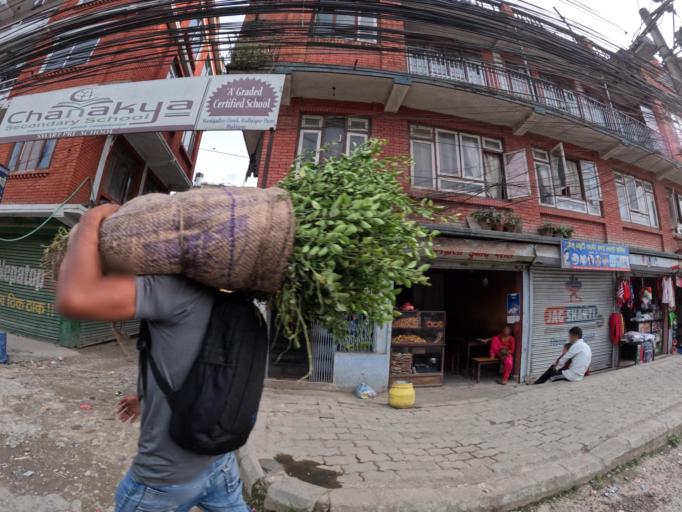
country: NP
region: Central Region
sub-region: Bagmati Zone
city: Bhaktapur
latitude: 27.6731
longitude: 85.3826
